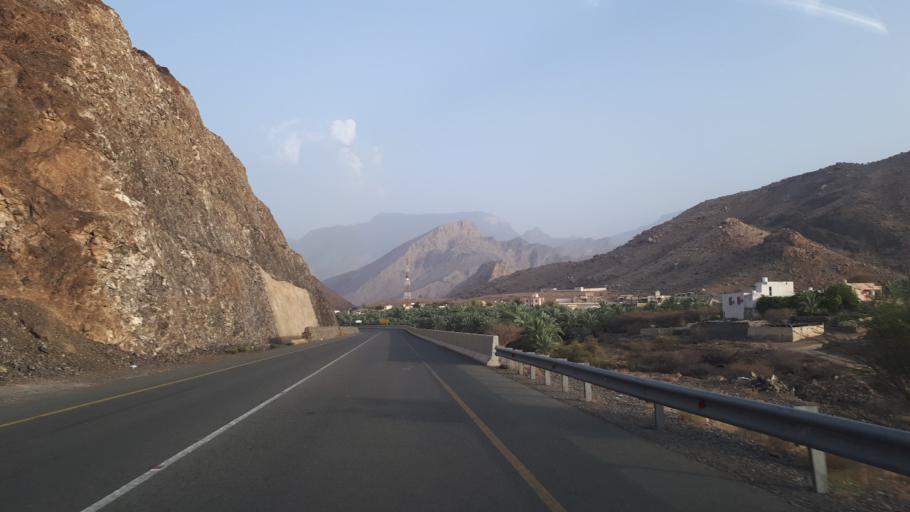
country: OM
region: Al Batinah
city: Rustaq
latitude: 23.4273
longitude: 57.1643
